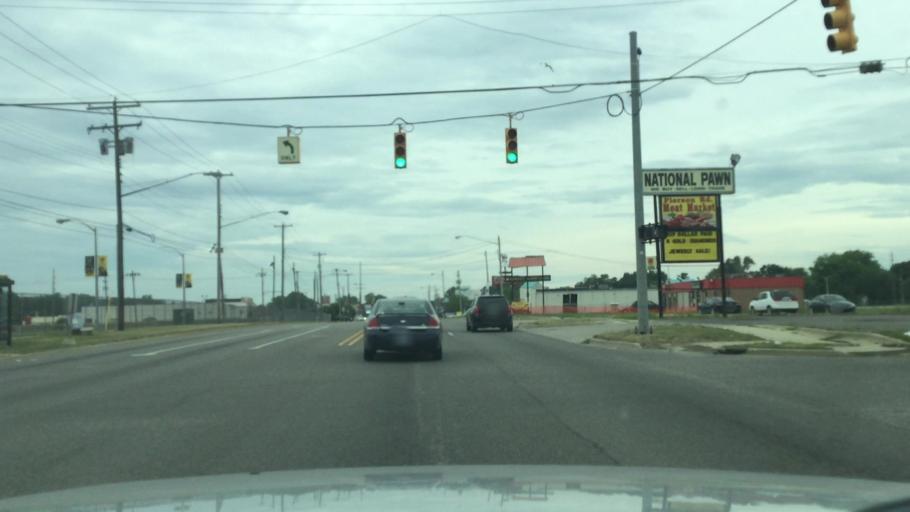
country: US
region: Michigan
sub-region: Genesee County
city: Beecher
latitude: 43.0607
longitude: -83.7296
